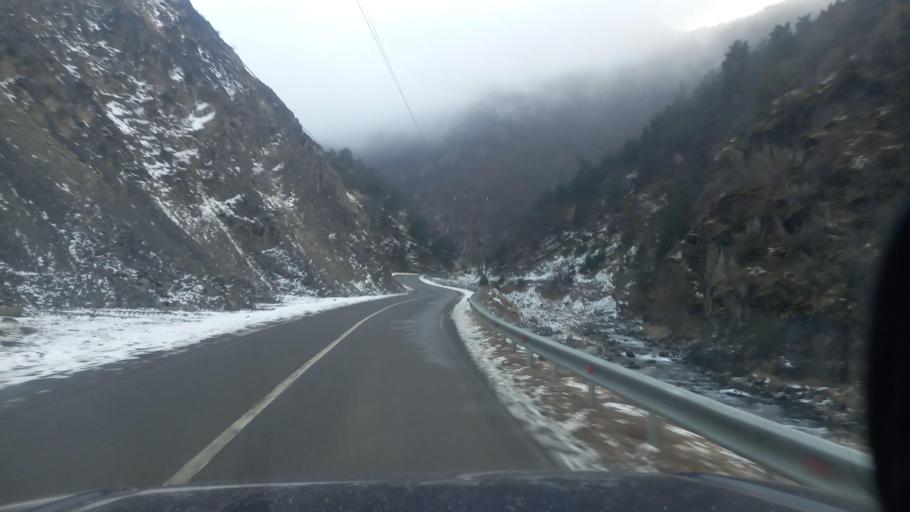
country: RU
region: Ingushetiya
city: Dzhayrakh
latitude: 42.7965
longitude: 44.7622
